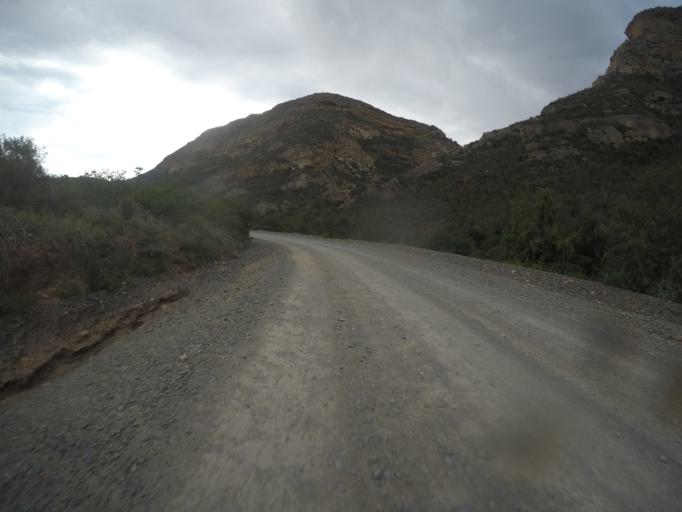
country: ZA
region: Eastern Cape
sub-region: Cacadu District Municipality
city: Willowmore
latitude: -33.5132
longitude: 23.8195
